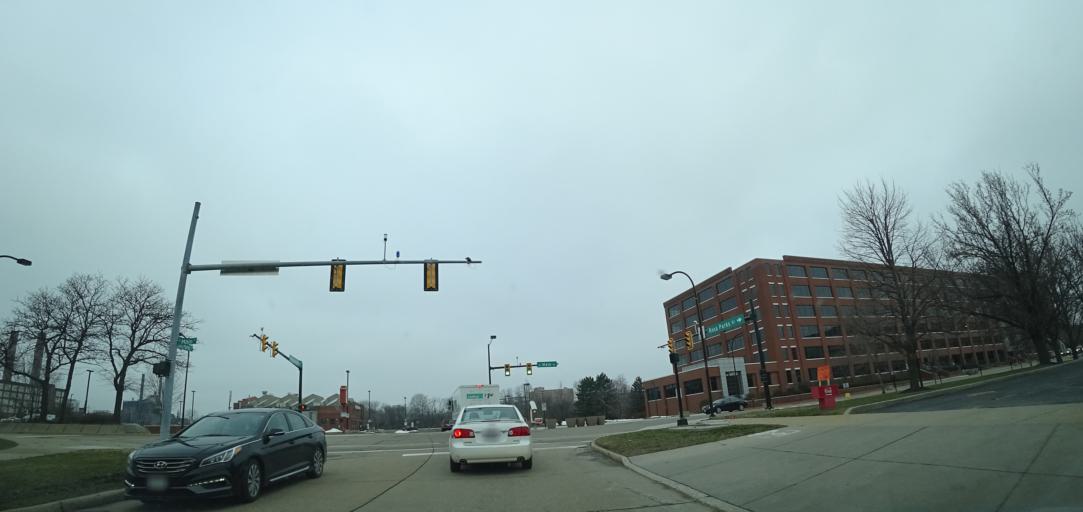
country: US
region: Ohio
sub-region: Summit County
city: Akron
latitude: 41.0734
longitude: -81.5238
